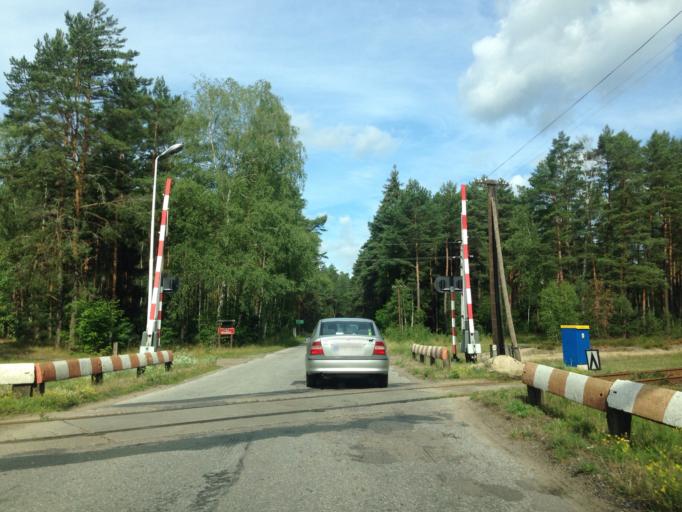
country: PL
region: Pomeranian Voivodeship
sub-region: Powiat starogardzki
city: Szlachta
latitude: 53.7442
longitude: 18.1131
